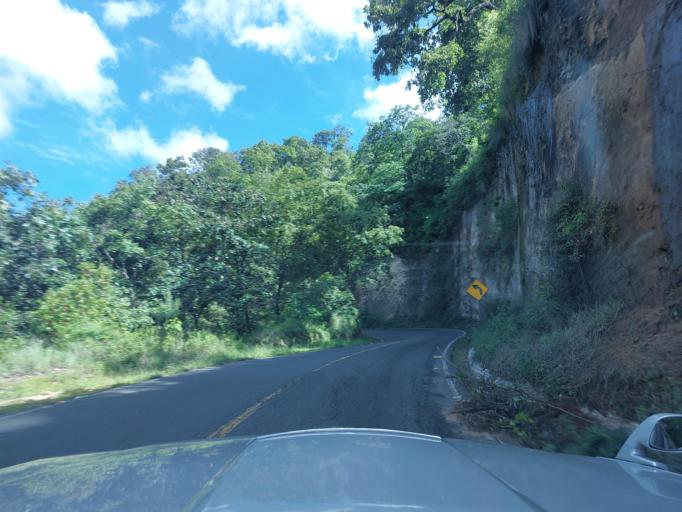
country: GT
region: Chimaltenango
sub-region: Municipio de Santa Cruz Balanya
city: Santa Cruz Balanya
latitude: 14.6964
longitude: -90.8989
